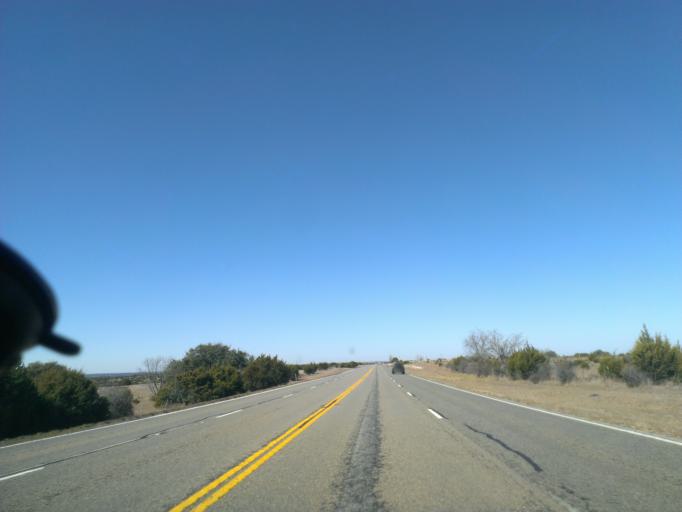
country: US
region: Texas
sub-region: Williamson County
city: Florence
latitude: 30.8953
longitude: -97.9620
